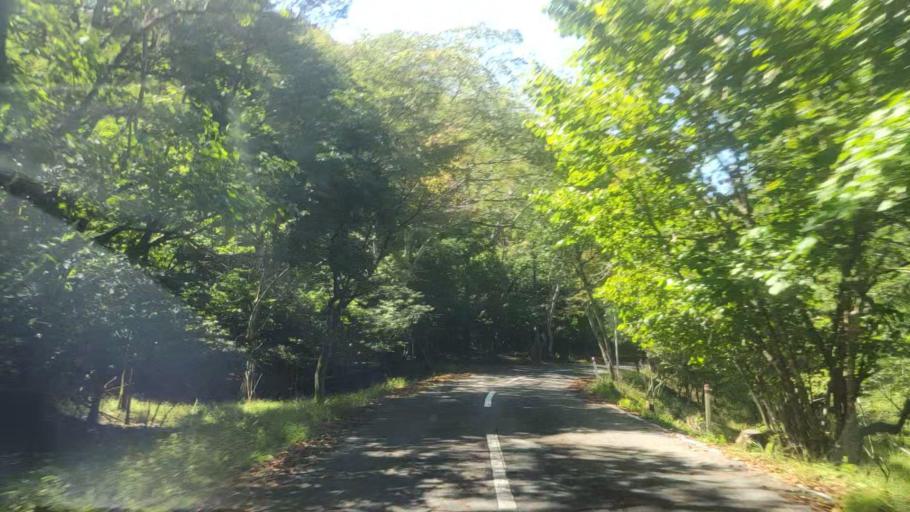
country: JP
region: Yamanashi
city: Fujikawaguchiko
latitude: 35.5706
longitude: 138.7751
